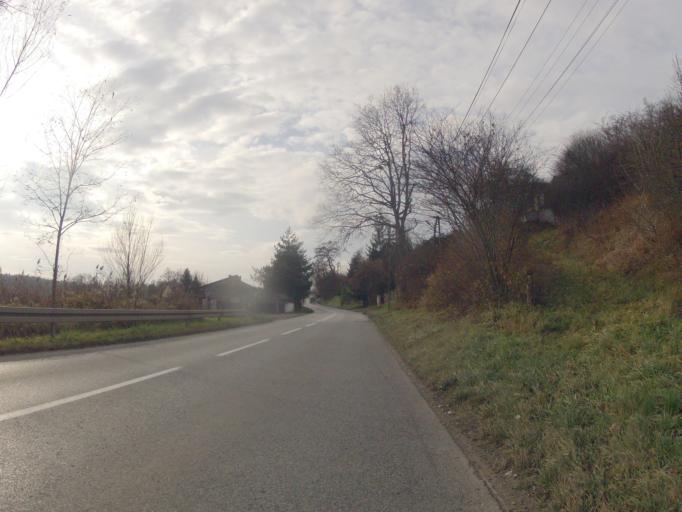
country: PL
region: Lesser Poland Voivodeship
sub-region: Powiat krakowski
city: Rzaska
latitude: 50.0893
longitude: 19.8206
